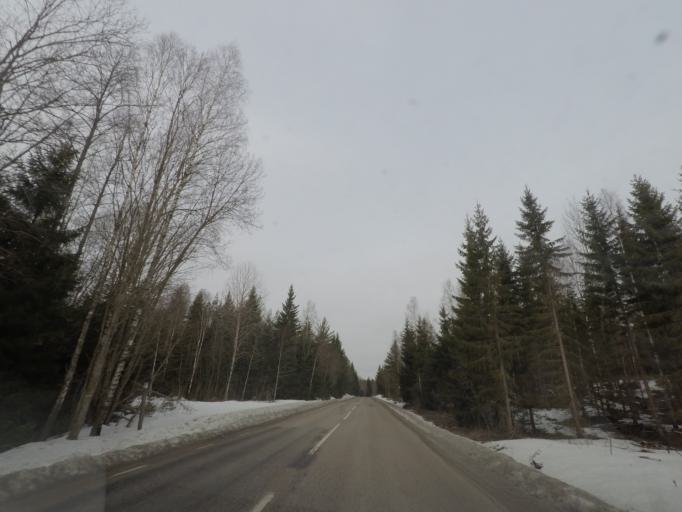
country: SE
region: Vaestmanland
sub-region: Vasteras
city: Skultuna
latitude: 59.7428
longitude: 16.3718
